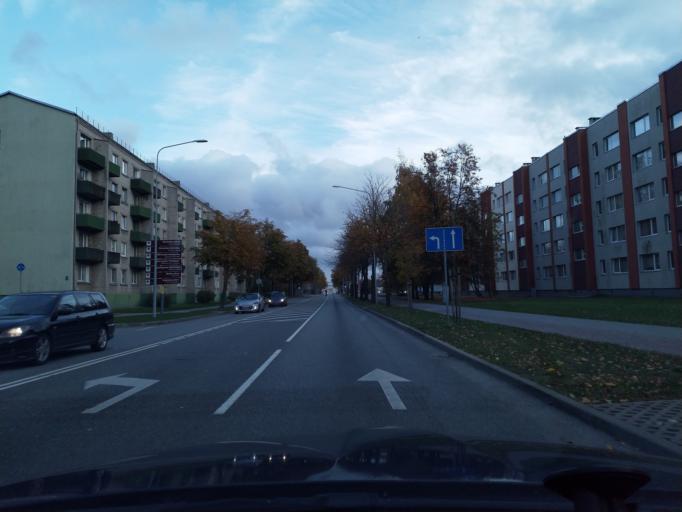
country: LV
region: Ventspils
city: Ventspils
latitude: 57.3894
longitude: 21.5755
